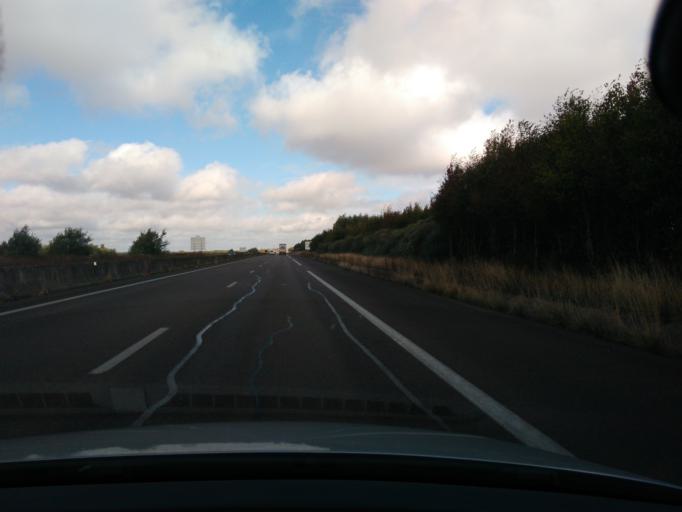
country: FR
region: Haute-Normandie
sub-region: Departement de l'Eure
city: Damville
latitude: 48.8740
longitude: 1.1755
